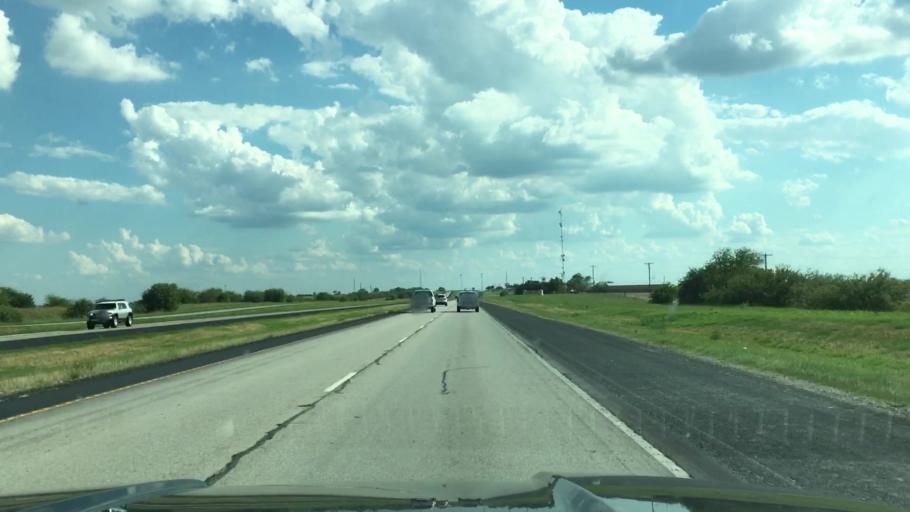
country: US
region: Texas
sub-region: Wise County
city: New Fairview
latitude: 33.0860
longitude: -97.4722
